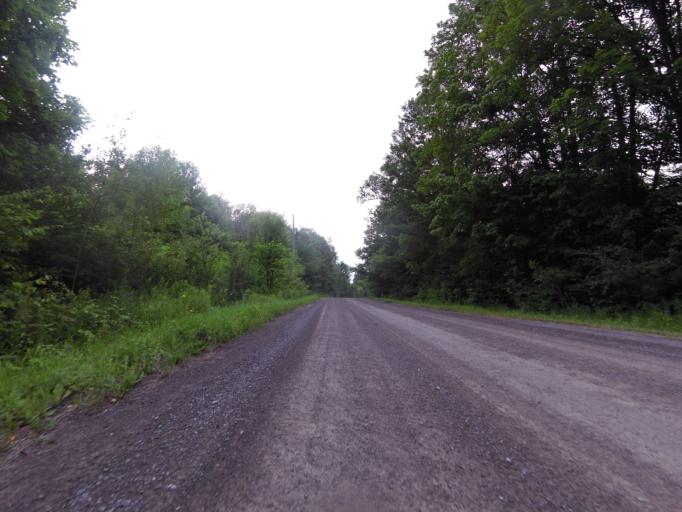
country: CA
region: Ontario
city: Carleton Place
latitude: 45.1654
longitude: -76.2745
